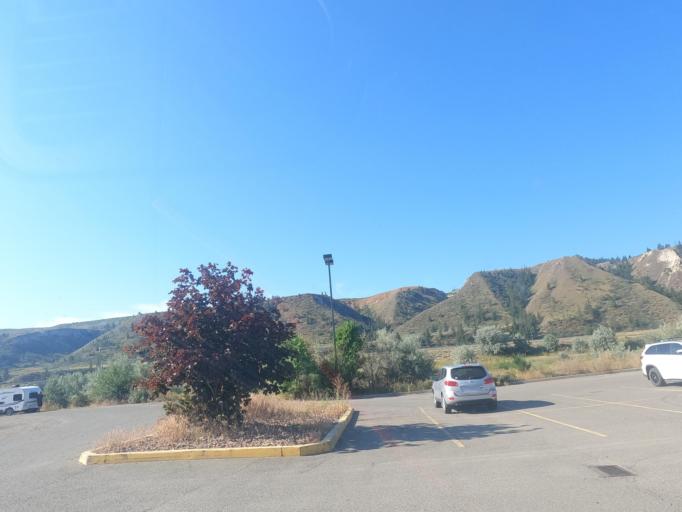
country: CA
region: British Columbia
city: Kamloops
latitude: 50.6610
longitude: -120.1198
